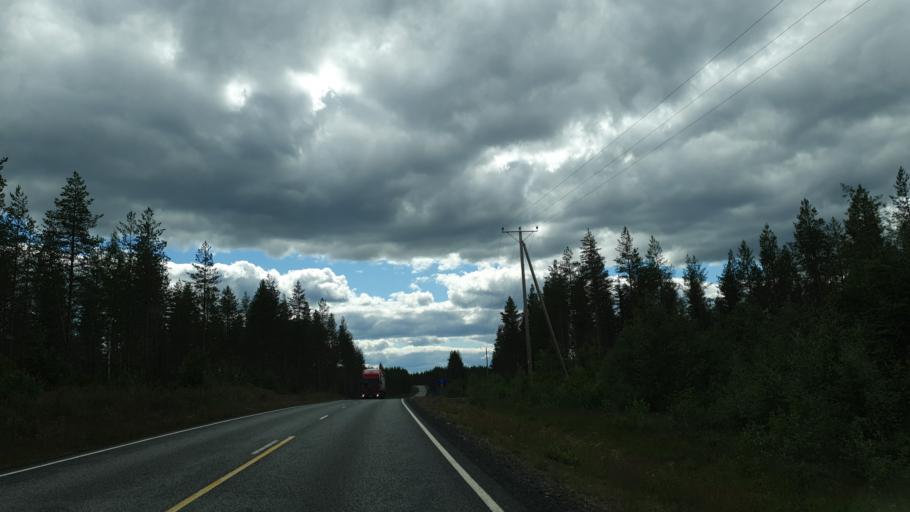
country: FI
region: Kainuu
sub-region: Kehys-Kainuu
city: Kuhmo
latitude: 64.0415
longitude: 29.5729
